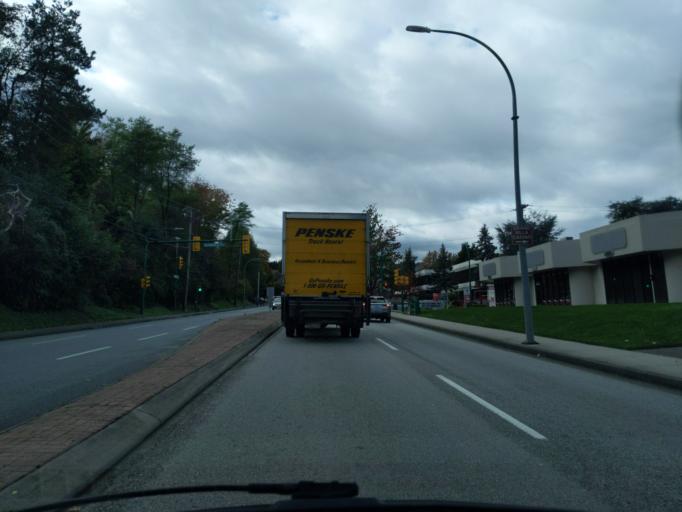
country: CA
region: British Columbia
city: Burnaby
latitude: 49.2547
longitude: -123.0075
